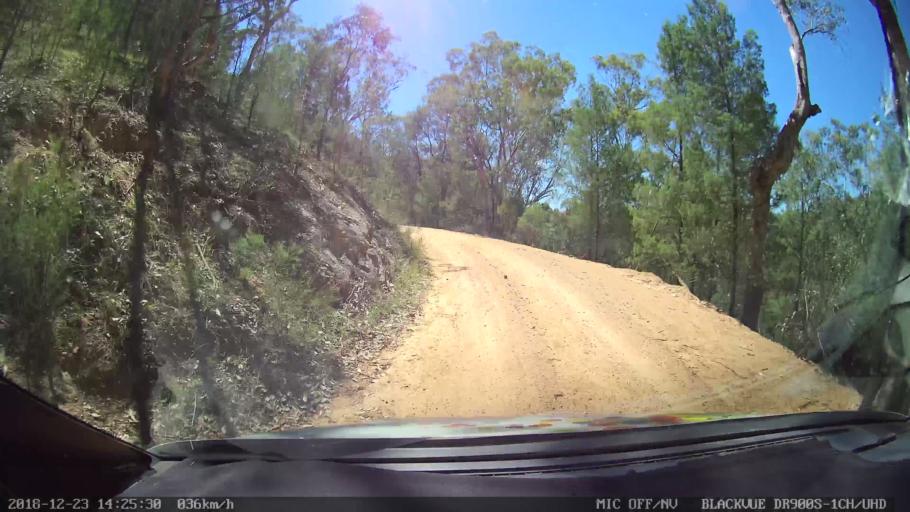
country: AU
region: New South Wales
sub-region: Tamworth Municipality
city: Manilla
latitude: -30.6266
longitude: 150.9555
